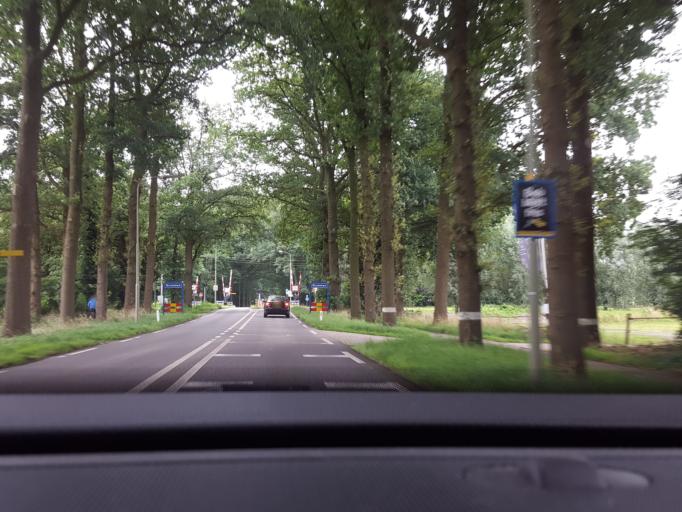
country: NL
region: Gelderland
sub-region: Gemeente Brummen
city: Brummen
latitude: 52.0891
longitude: 6.1445
